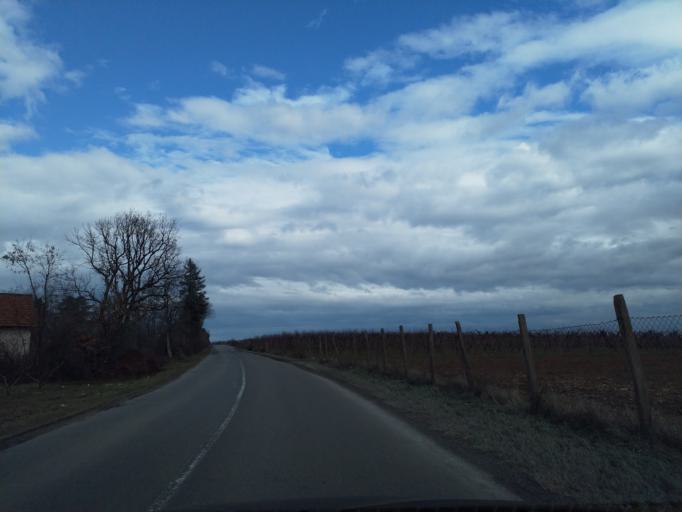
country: RS
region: Central Serbia
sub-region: Belgrade
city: Grocka
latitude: 44.6333
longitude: 20.7492
